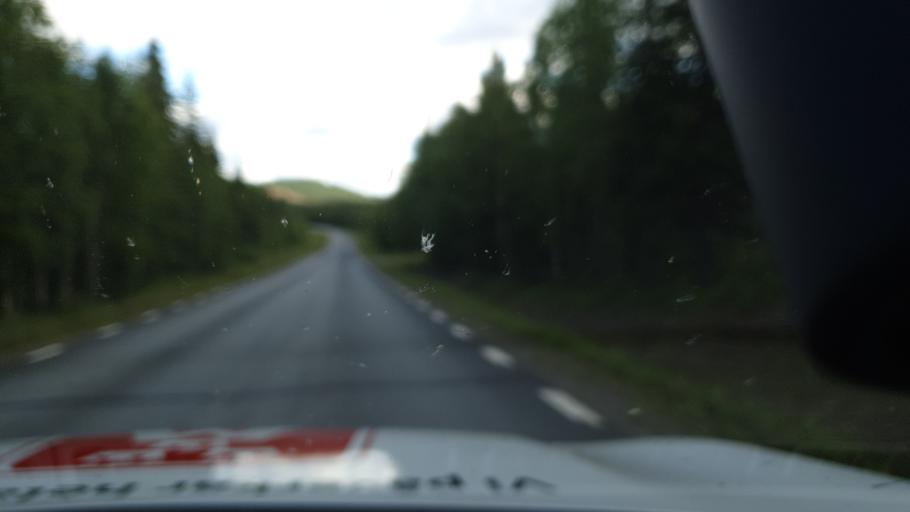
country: SE
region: Vaesterbotten
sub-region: Mala Kommun
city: Mala
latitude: 65.1494
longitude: 18.6632
